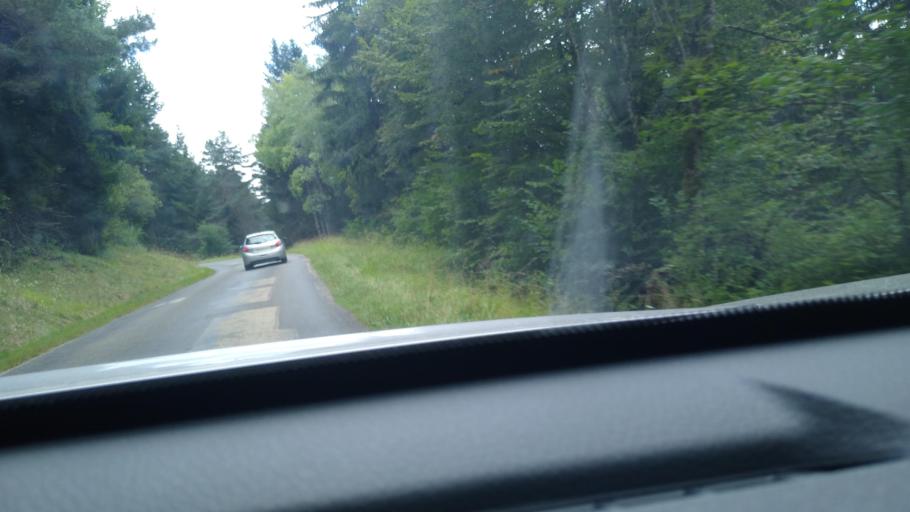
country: FR
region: Rhone-Alpes
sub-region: Departement de l'Ain
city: Saint-Martin-du-Frene
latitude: 46.1327
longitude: 5.5566
